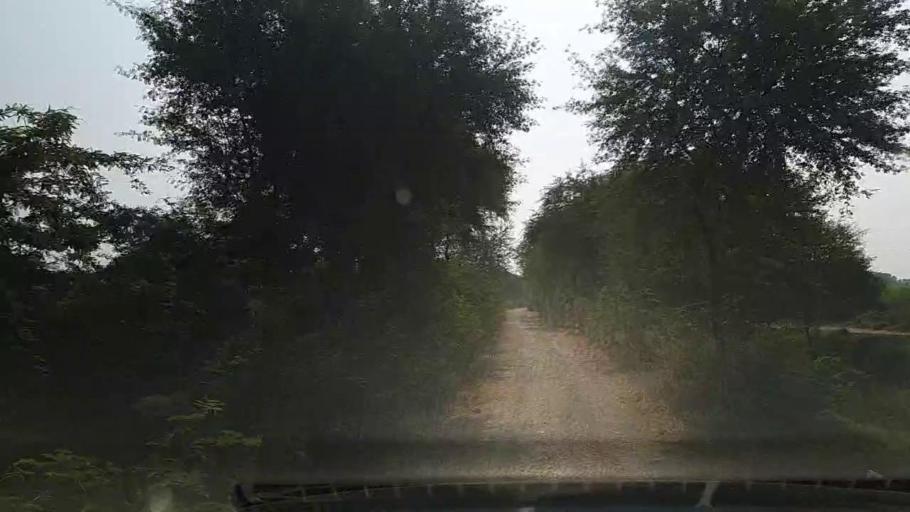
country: PK
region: Sindh
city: Mirpur Batoro
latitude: 24.6878
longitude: 68.2219
